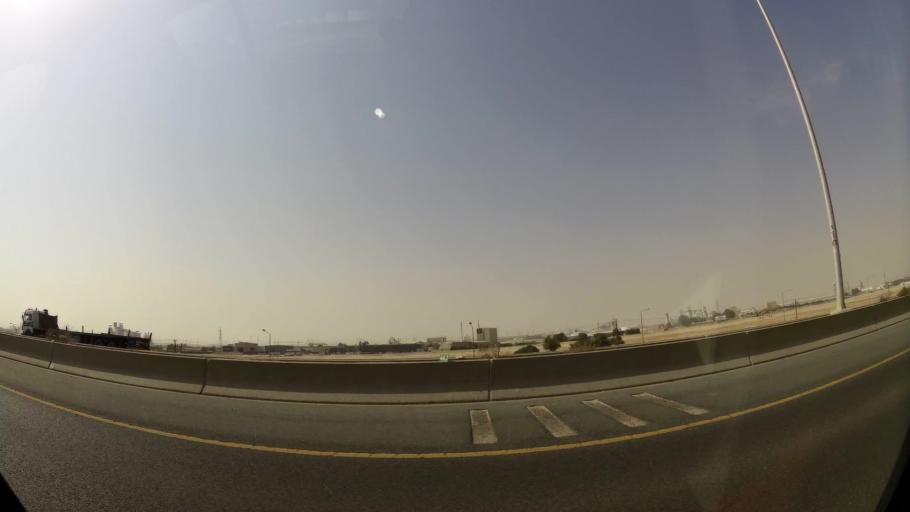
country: KW
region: Al Ahmadi
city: Al Fahahil
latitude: 29.0129
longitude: 48.1316
